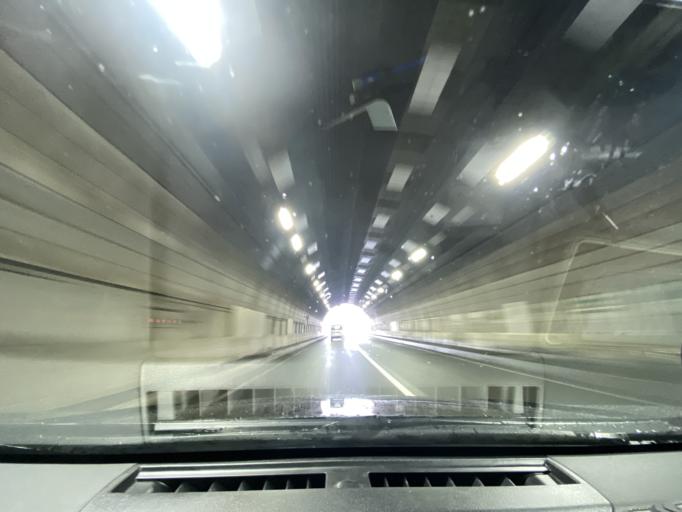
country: JP
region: Hokkaido
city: Fukagawa
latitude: 43.7292
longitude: 142.2029
